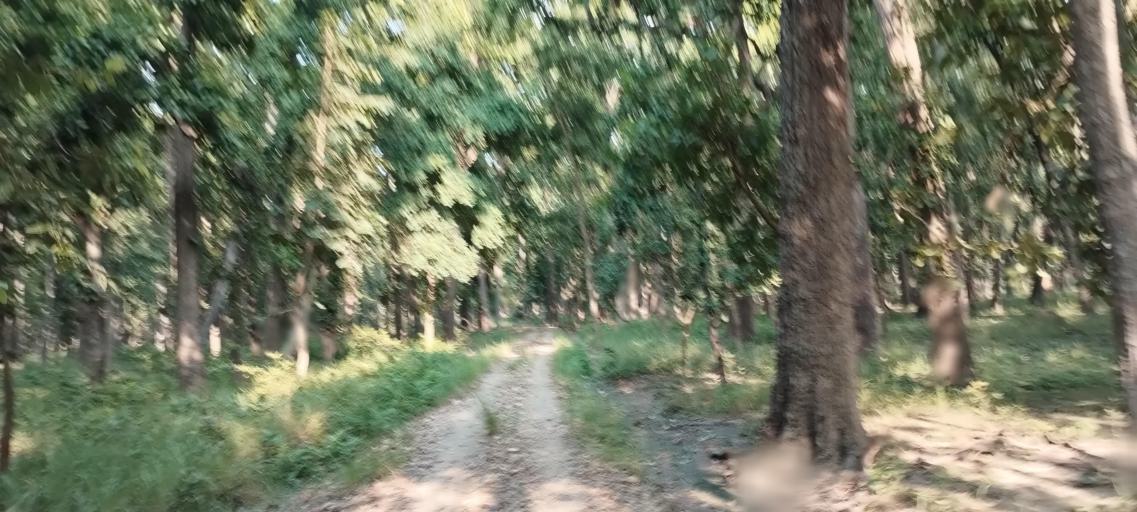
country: NP
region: Far Western
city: Tikapur
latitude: 28.5188
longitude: 81.2805
